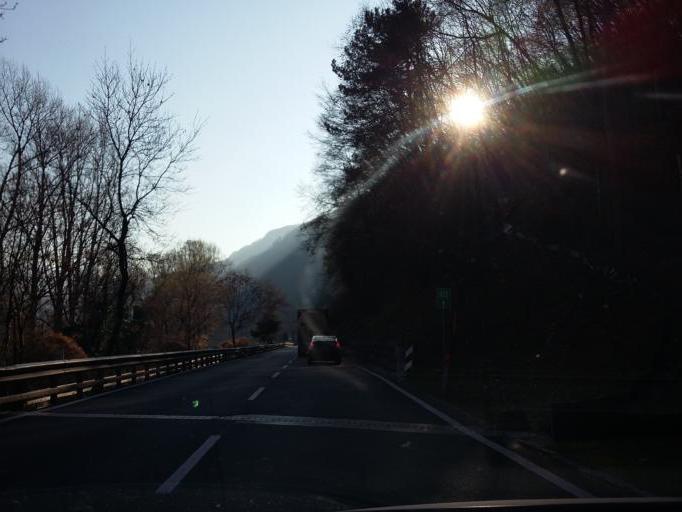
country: IT
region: Trentino-Alto Adige
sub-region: Provincia di Trento
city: Nago-Torbole
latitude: 45.8603
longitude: 10.9185
